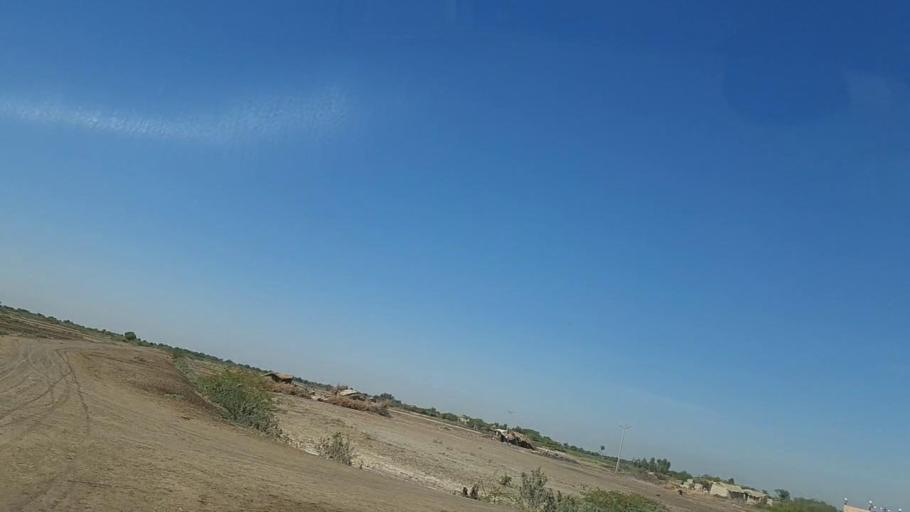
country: PK
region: Sindh
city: Dhoro Naro
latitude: 25.4893
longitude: 69.5097
